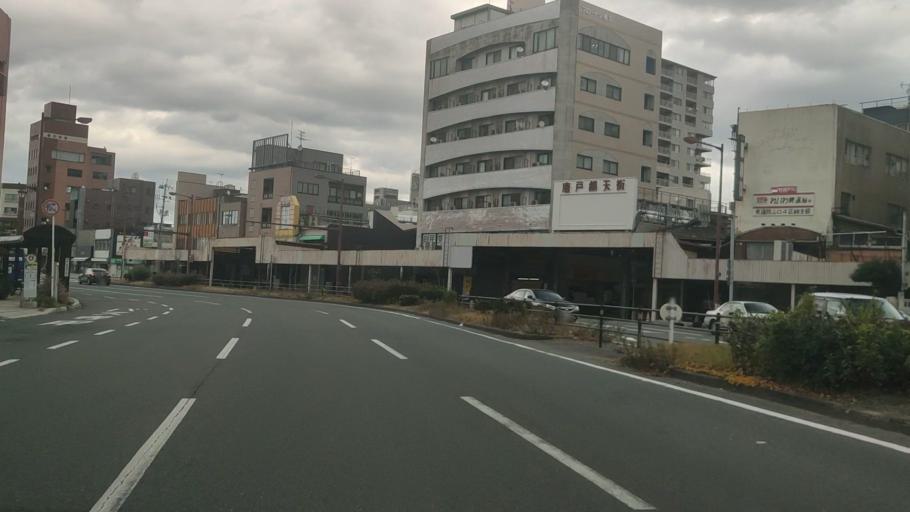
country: JP
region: Yamaguchi
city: Shimonoseki
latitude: 33.9570
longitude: 130.9424
